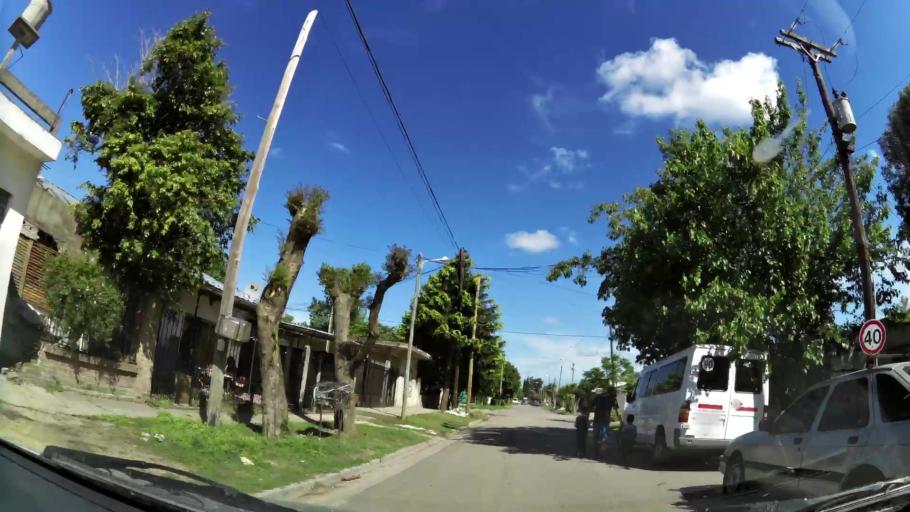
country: AR
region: Buenos Aires
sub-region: Partido de Quilmes
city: Quilmes
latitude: -34.8024
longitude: -58.2479
